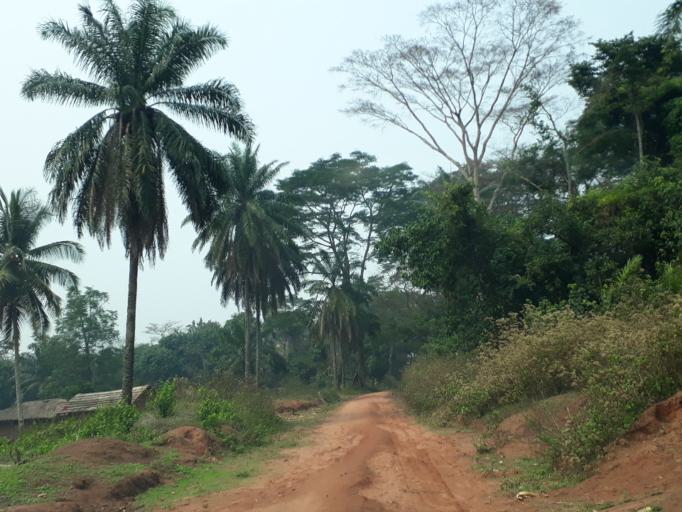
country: CD
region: Kasai-Occidental
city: Tshikapa
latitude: -6.1646
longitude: 20.4226
